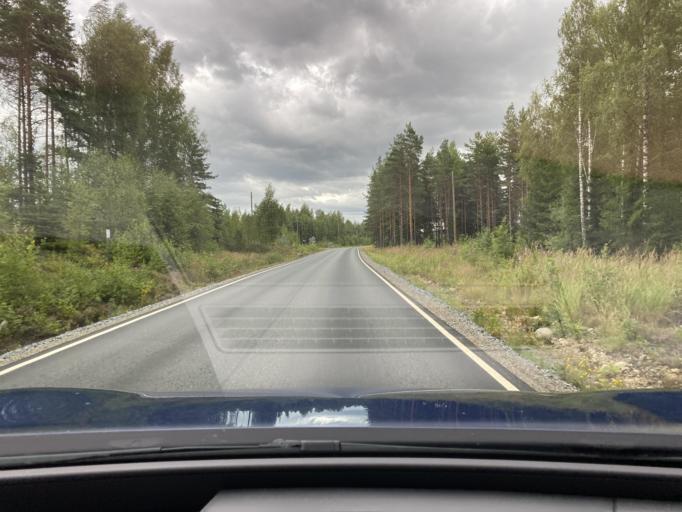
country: FI
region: Pirkanmaa
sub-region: Lounais-Pirkanmaa
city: Punkalaidun
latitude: 61.2714
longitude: 23.0688
